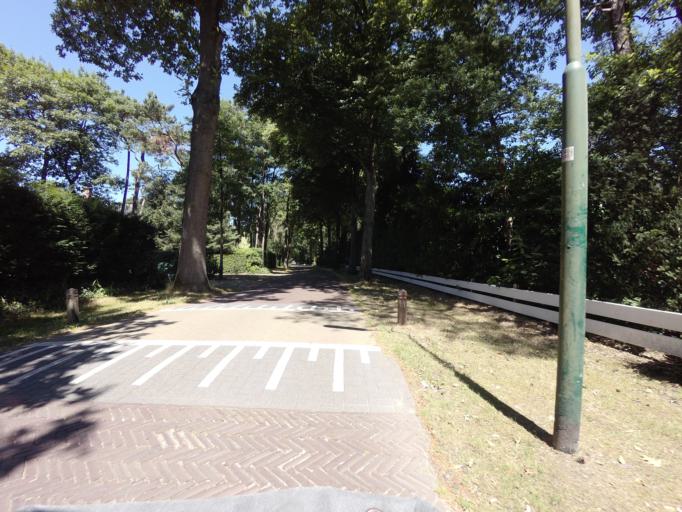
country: NL
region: Utrecht
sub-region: Gemeente Zeist
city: Zeist
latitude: 52.1398
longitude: 5.2271
